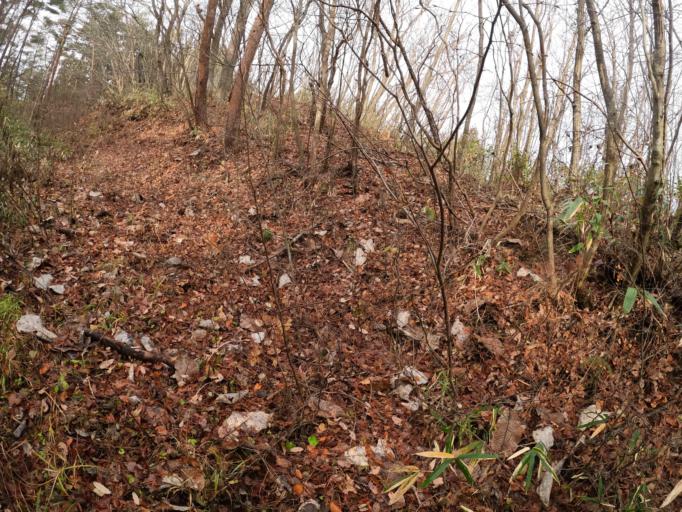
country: JP
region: Iwate
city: Ichinoseki
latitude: 38.8825
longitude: 141.1308
